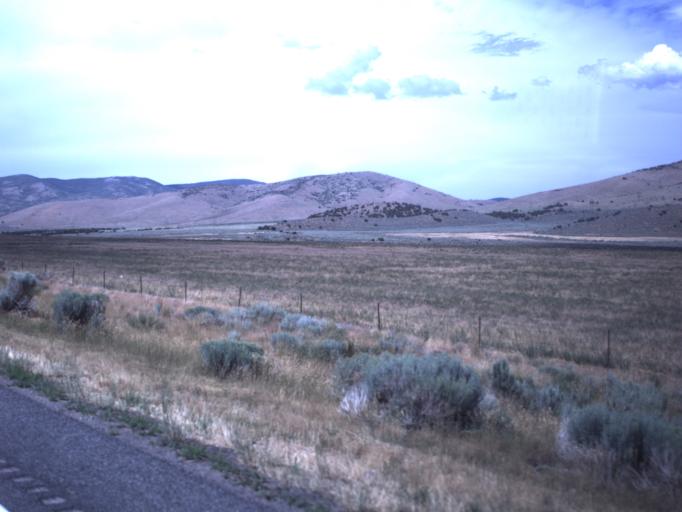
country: US
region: Utah
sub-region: Sanpete County
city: Fountain Green
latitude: 39.6522
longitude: -111.6489
